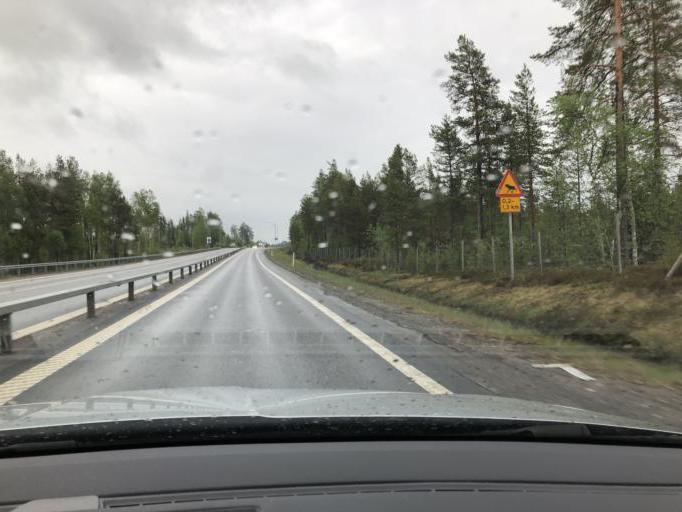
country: SE
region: Vaesterbotten
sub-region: Umea Kommun
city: Hoernefors
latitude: 63.6127
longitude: 19.7987
